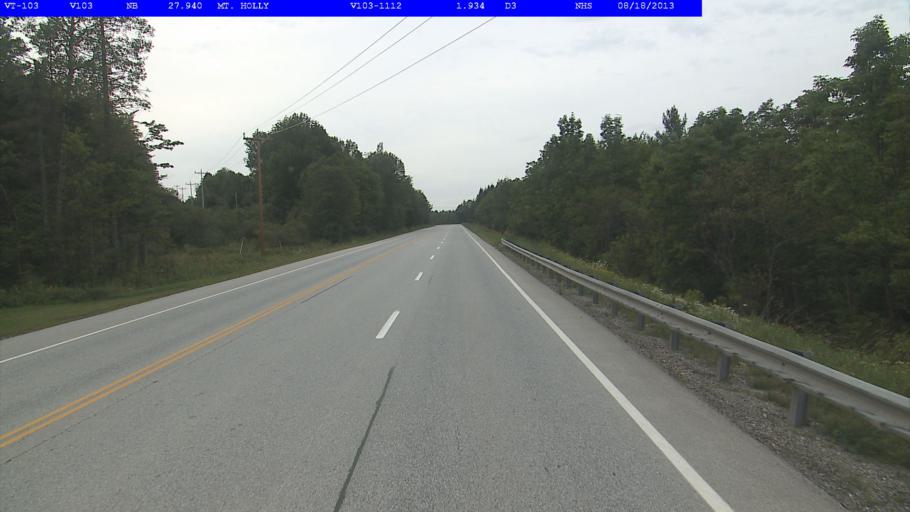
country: US
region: Vermont
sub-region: Windsor County
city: Chester
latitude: 43.4430
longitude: -72.7683
